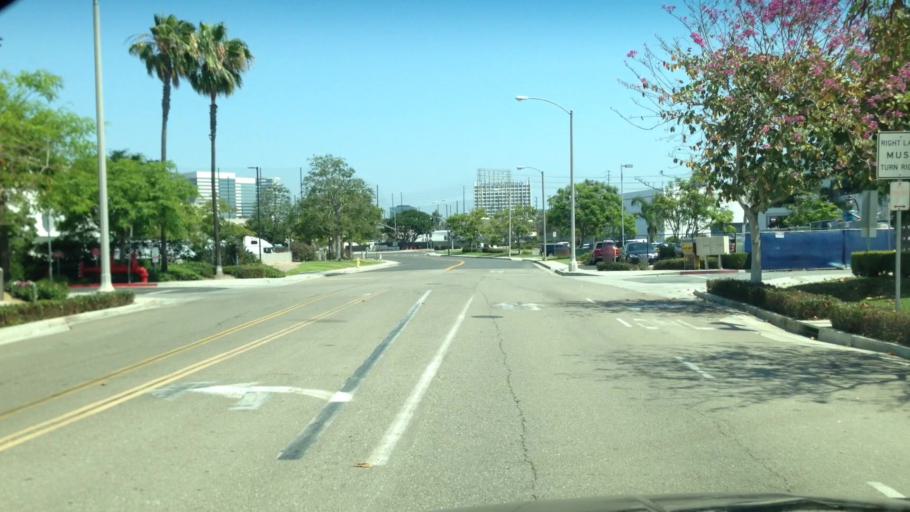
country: US
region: California
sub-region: Los Angeles County
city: Del Aire
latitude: 33.9067
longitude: -118.3915
